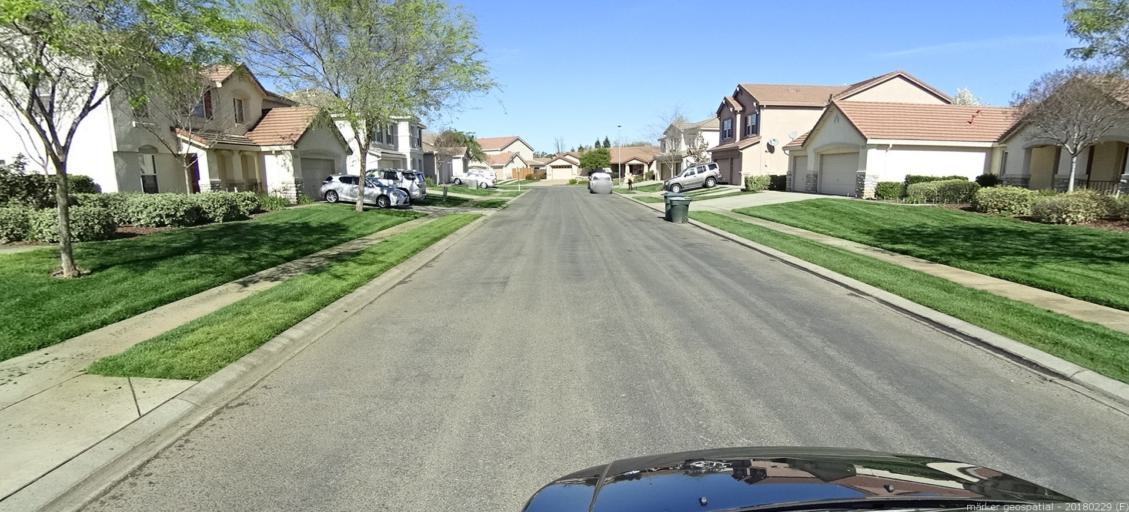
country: US
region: California
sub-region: Sacramento County
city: Rancho Cordova
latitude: 38.5462
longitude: -121.2747
